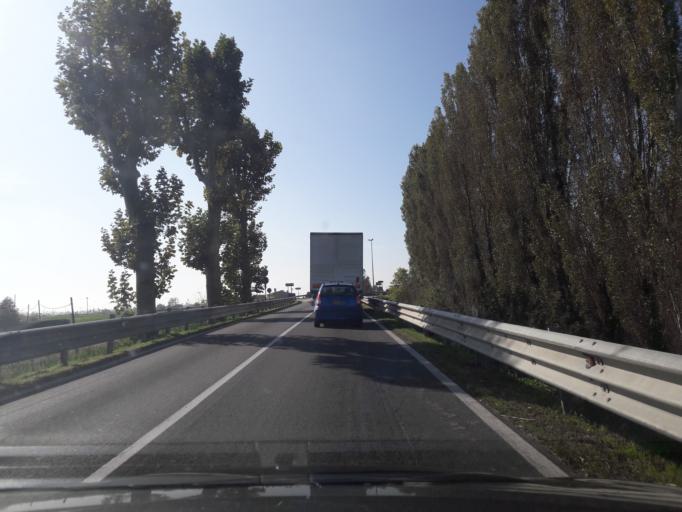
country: IT
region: Veneto
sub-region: Provincia di Venezia
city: Cavarzere
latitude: 45.1000
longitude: 12.0576
